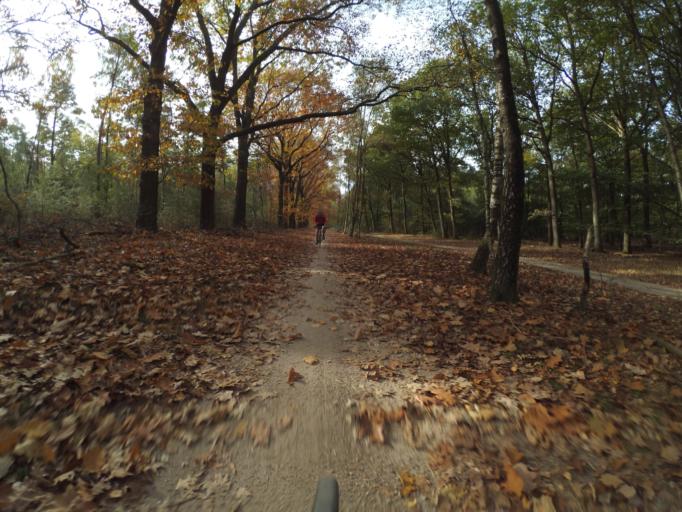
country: NL
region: Overijssel
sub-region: Gemeente Raalte
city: Raalte
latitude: 52.3574
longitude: 6.4014
